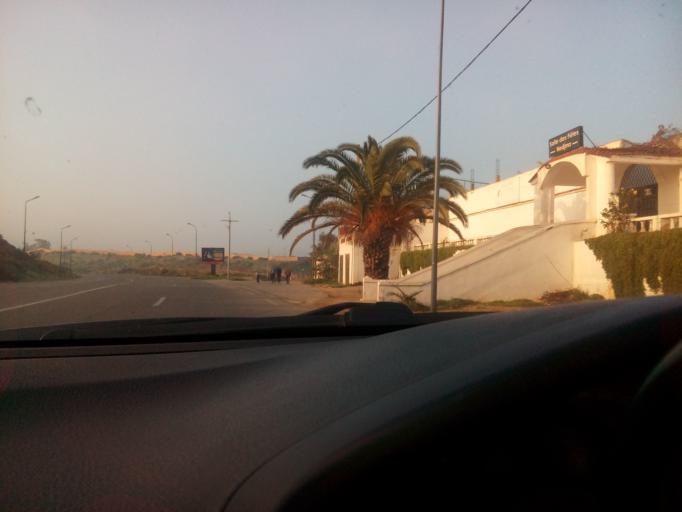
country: DZ
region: Oran
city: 'Ain el Turk
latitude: 35.7213
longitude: -0.8506
